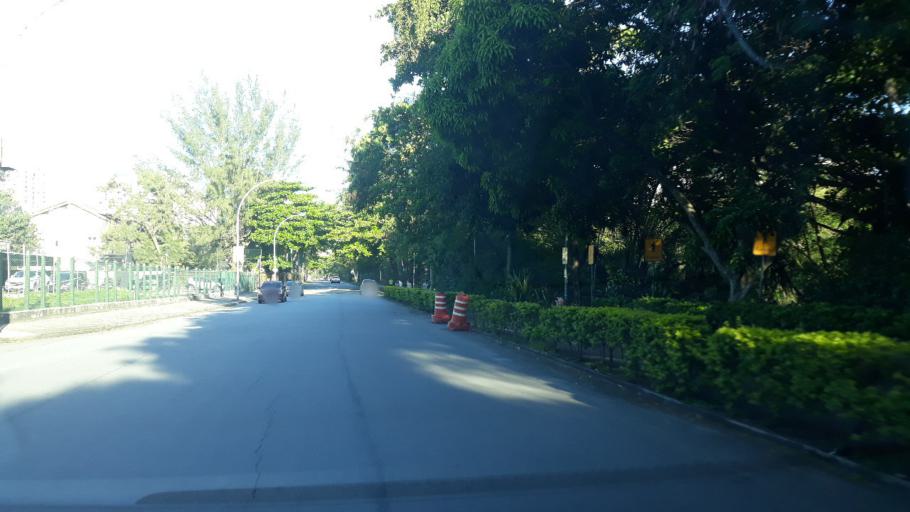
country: BR
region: Rio de Janeiro
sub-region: Rio De Janeiro
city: Rio de Janeiro
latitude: -23.0057
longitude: -43.3473
